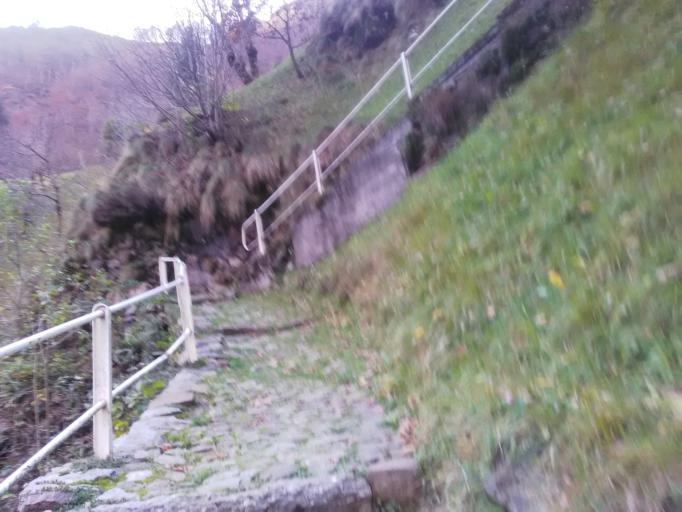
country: IT
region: Piedmont
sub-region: Provincia di Vercelli
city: Cervatto
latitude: 45.8838
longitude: 8.1770
